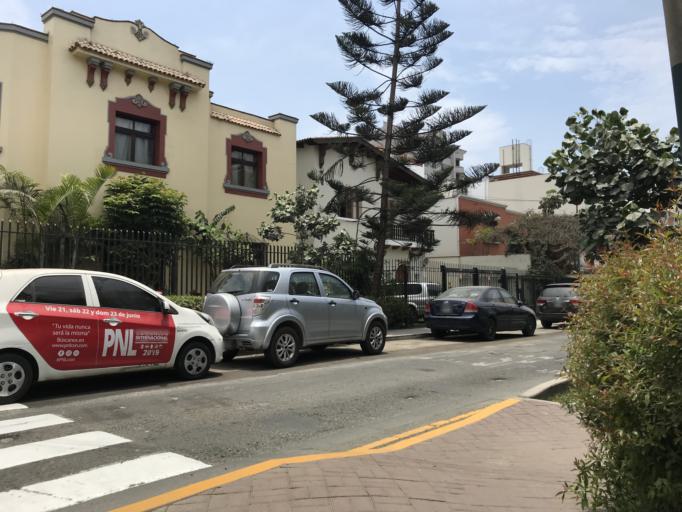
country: PE
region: Lima
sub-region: Lima
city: San Isidro
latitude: -12.0919
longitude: -77.0518
